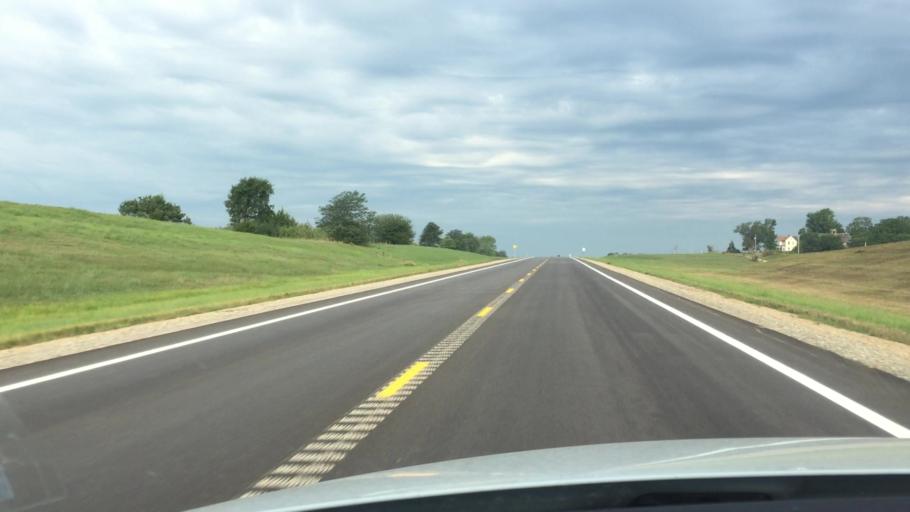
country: US
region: Kansas
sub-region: Doniphan County
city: Highland
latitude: 39.8412
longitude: -95.3855
